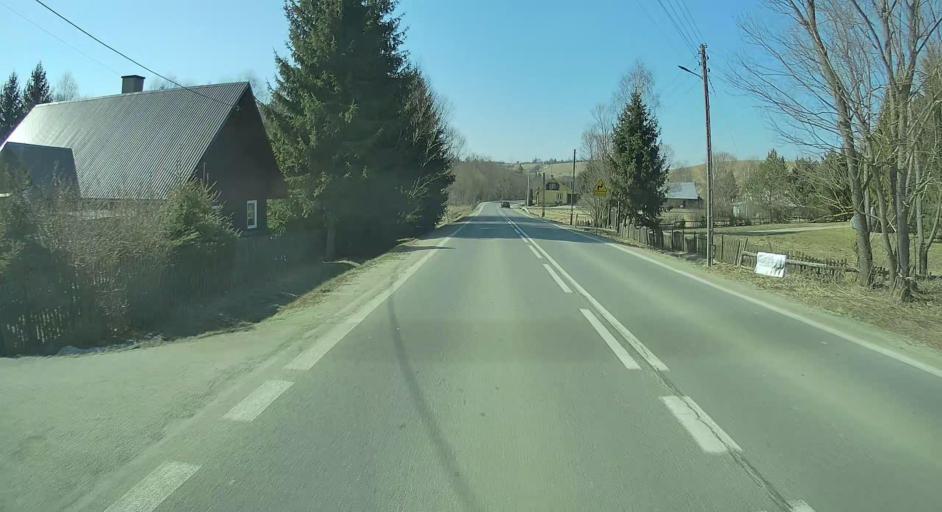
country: PL
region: Subcarpathian Voivodeship
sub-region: Powiat bieszczadzki
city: Ustrzyki Dolne
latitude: 49.4922
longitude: 22.6434
